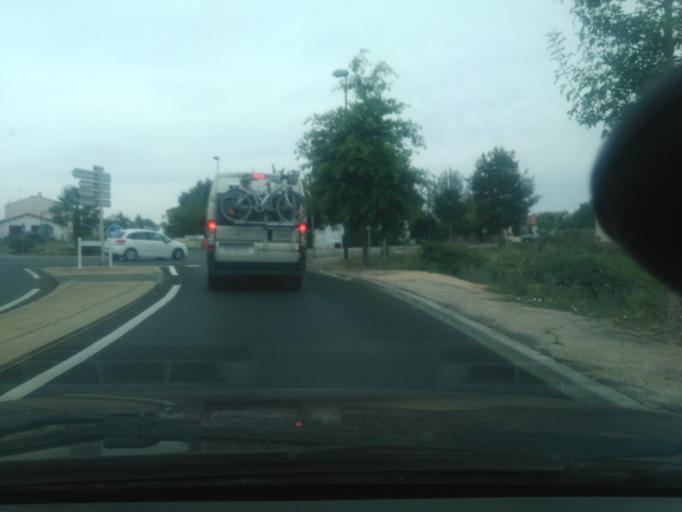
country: FR
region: Pays de la Loire
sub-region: Departement de la Vendee
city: Mouilleron-en-Pareds
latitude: 46.6773
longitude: -0.8547
